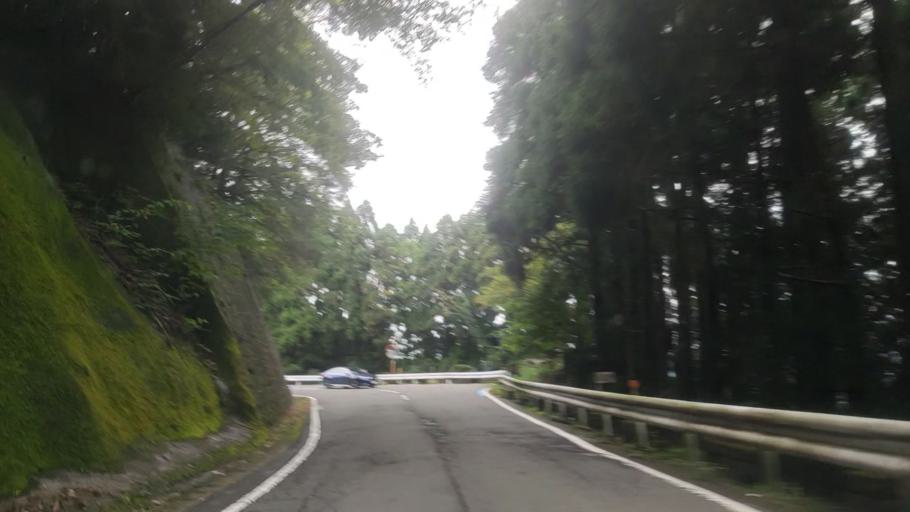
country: JP
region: Wakayama
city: Koya
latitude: 34.2100
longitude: 135.5430
